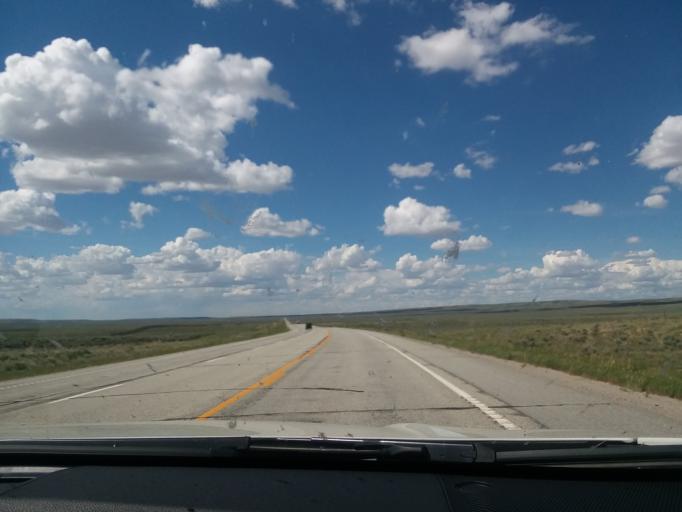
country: US
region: Wyoming
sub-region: Sweetwater County
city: North Rock Springs
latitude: 41.7916
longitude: -109.3340
